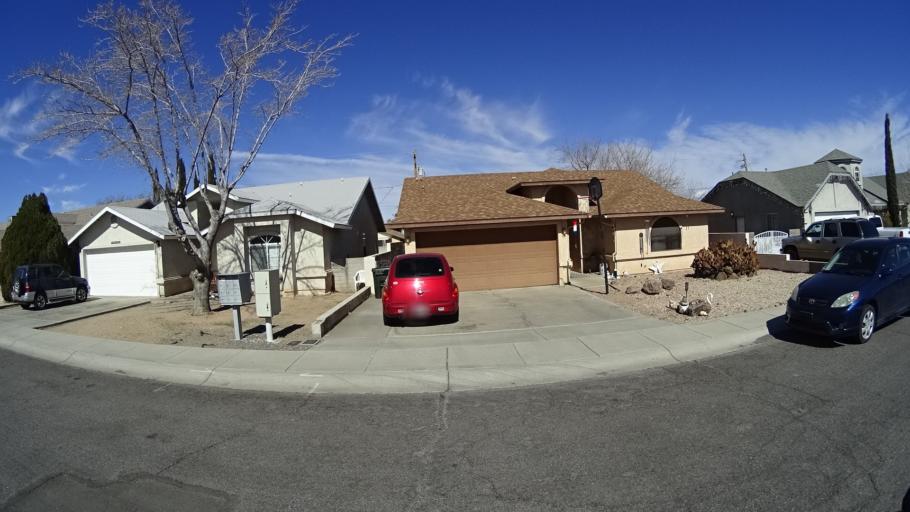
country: US
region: Arizona
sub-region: Mohave County
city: Kingman
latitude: 35.2111
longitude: -114.0364
